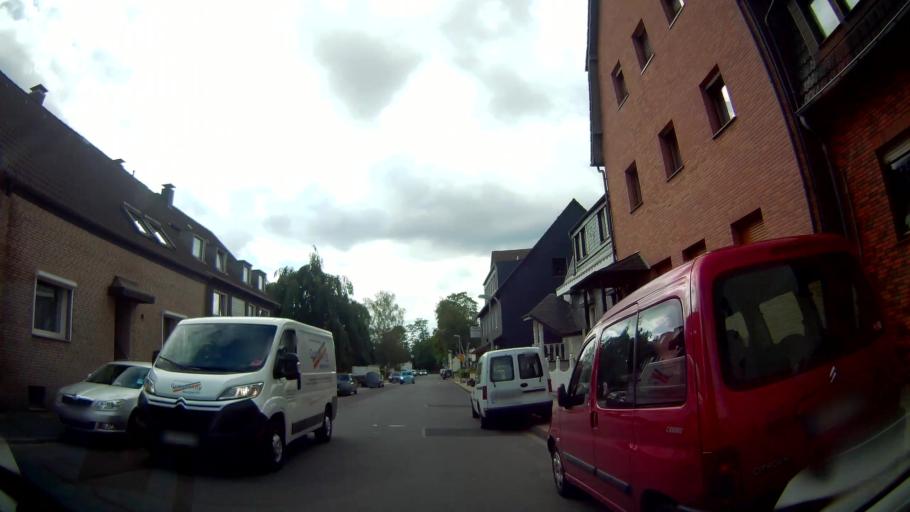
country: DE
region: North Rhine-Westphalia
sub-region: Regierungsbezirk Munster
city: Bottrop
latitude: 51.4918
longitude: 6.9380
